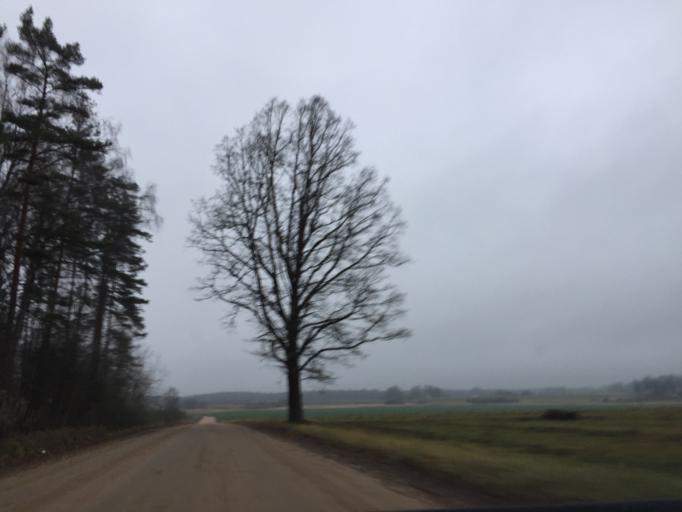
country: LV
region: Koceni
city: Koceni
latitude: 57.5437
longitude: 25.3288
